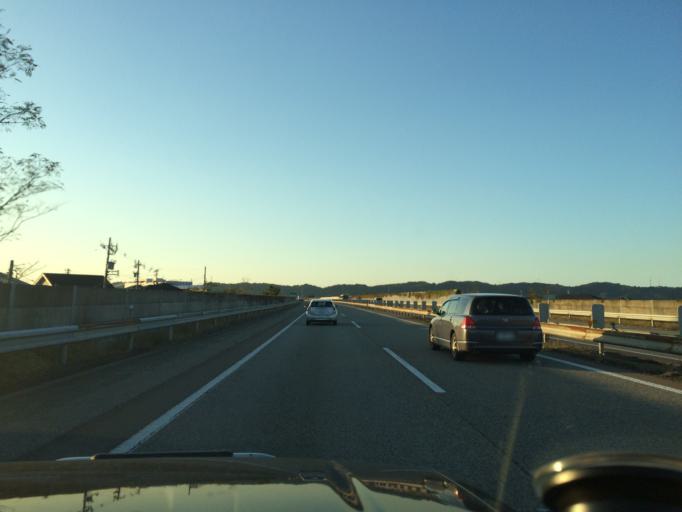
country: JP
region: Toyama
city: Toyama-shi
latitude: 36.6693
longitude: 137.1806
